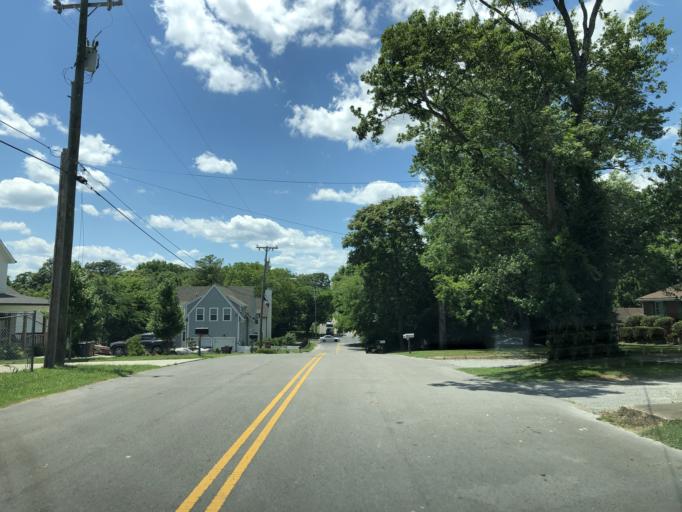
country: US
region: Tennessee
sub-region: Davidson County
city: Nashville
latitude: 36.1880
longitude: -86.7251
